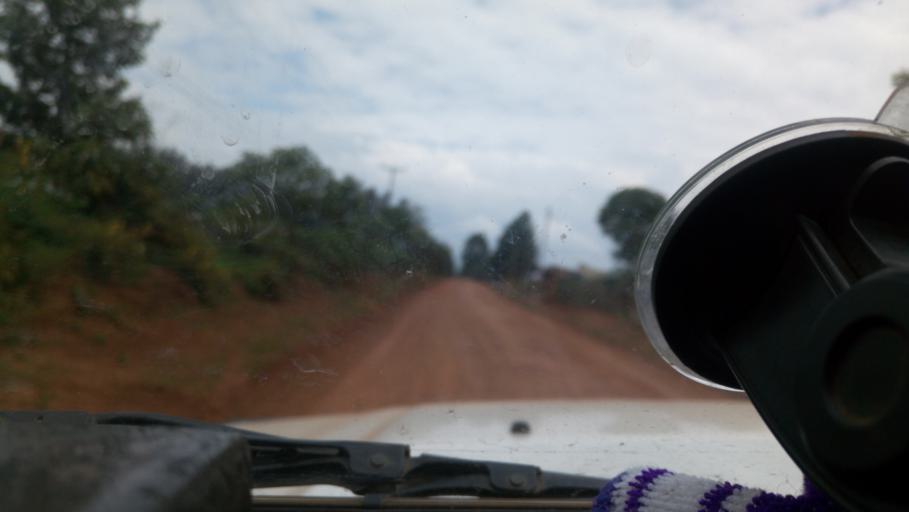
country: KE
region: Kericho
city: Litein
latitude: -0.6006
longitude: 35.1852
